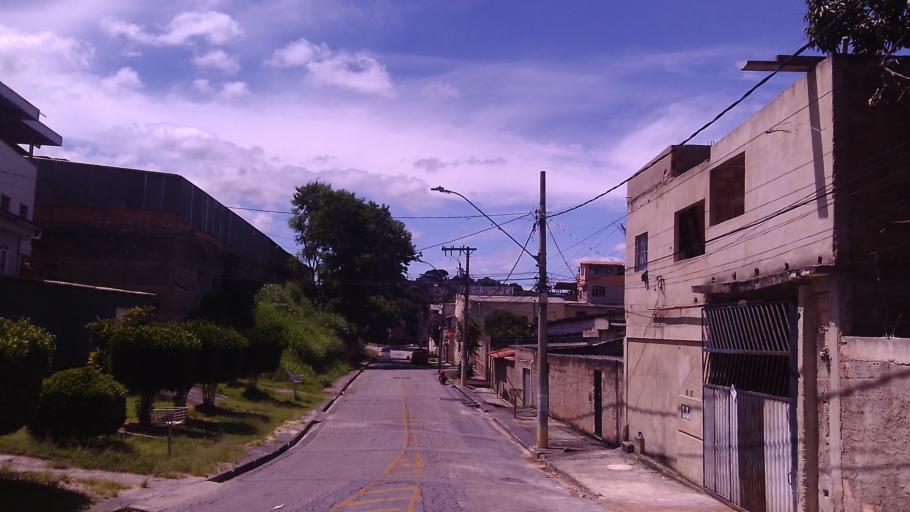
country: BR
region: Minas Gerais
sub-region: Belo Horizonte
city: Belo Horizonte
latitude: -19.8588
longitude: -43.9069
